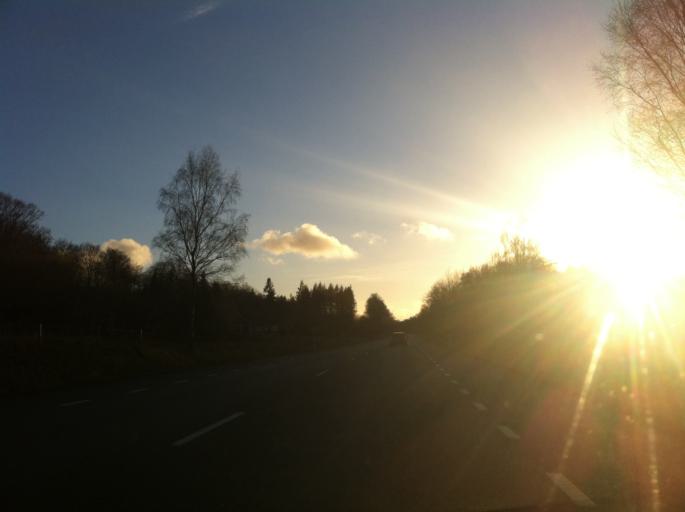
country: SE
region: Skane
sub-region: Hassleholms Kommun
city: Hassleholm
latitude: 56.1586
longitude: 13.8190
